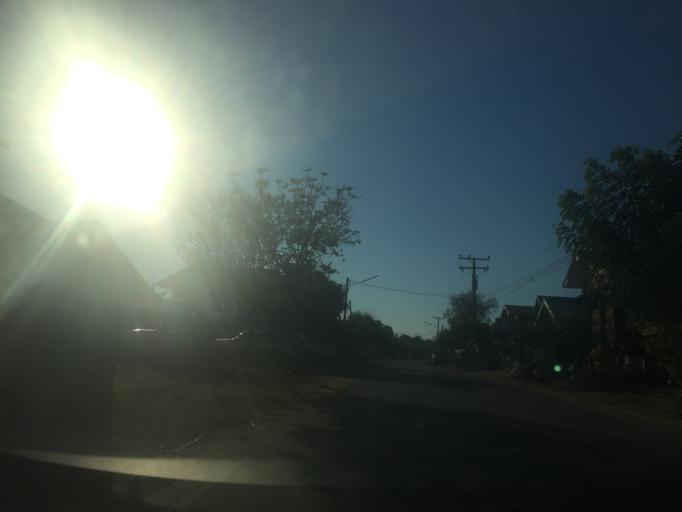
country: TH
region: Kalasin
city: Tha Khantho
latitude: 16.9806
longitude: 103.2715
